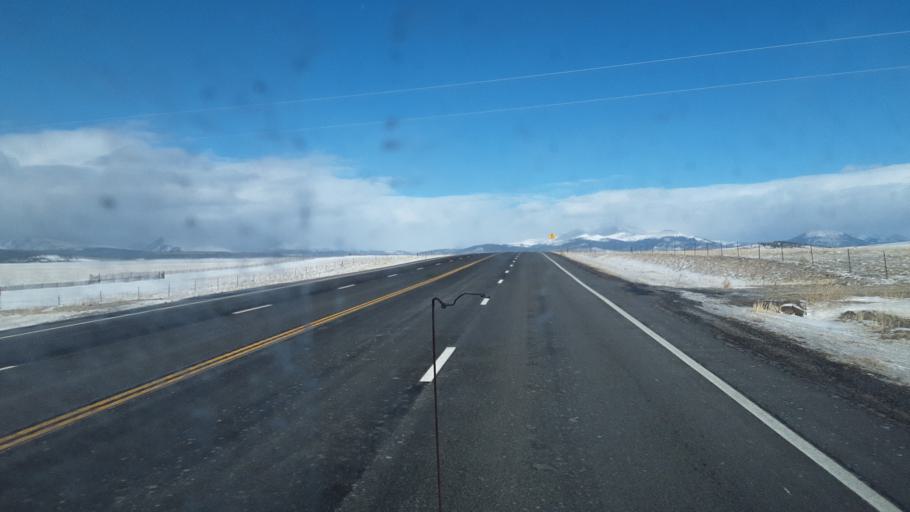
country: US
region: Colorado
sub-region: Park County
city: Fairplay
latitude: 39.1432
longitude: -105.9976
